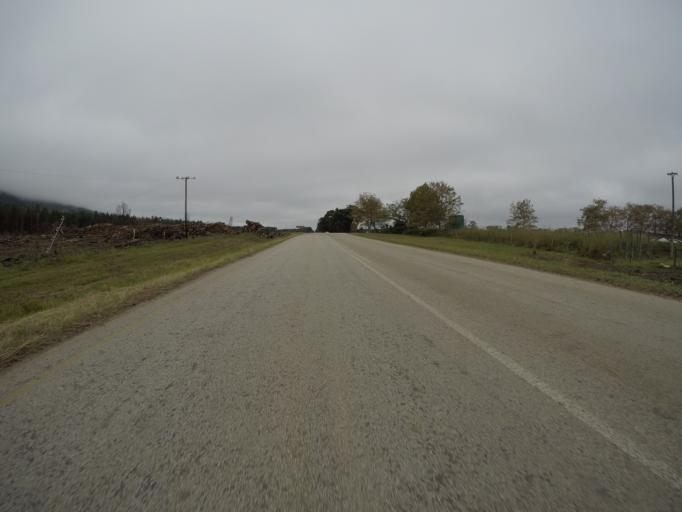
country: ZA
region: Eastern Cape
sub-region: Cacadu District Municipality
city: Kareedouw
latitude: -33.9877
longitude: 24.0735
